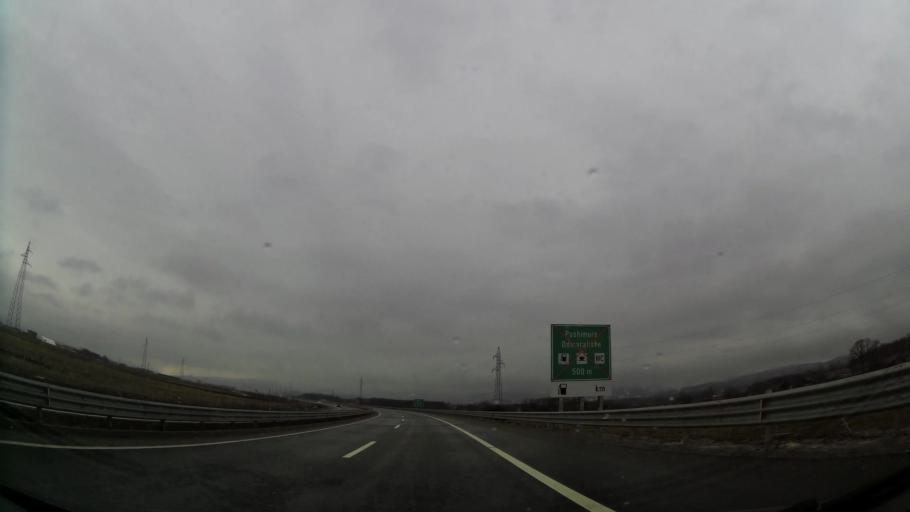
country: XK
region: Ferizaj
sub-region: Komuna e Kacanikut
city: Kacanik
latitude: 42.2984
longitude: 21.2041
